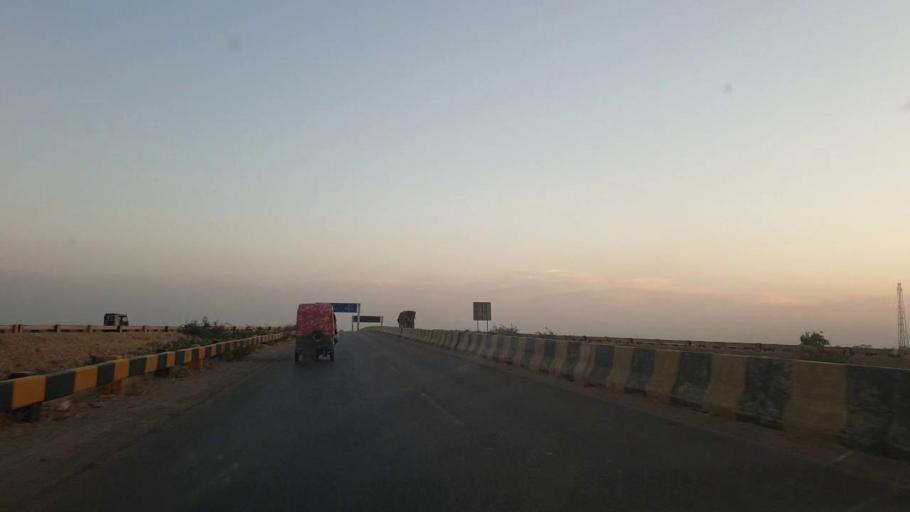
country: PK
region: Sindh
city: Jamshoro
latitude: 25.4018
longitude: 68.2724
